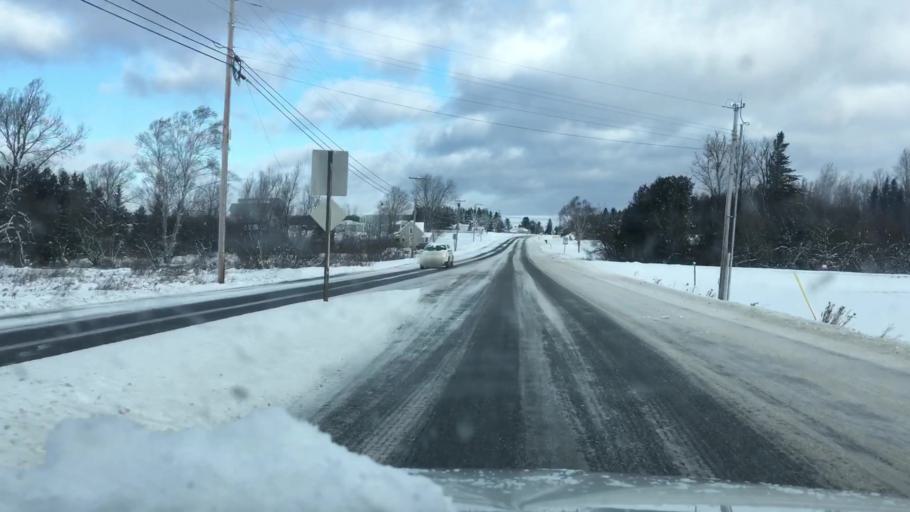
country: US
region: Maine
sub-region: Aroostook County
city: Caribou
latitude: 46.8883
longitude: -68.0143
